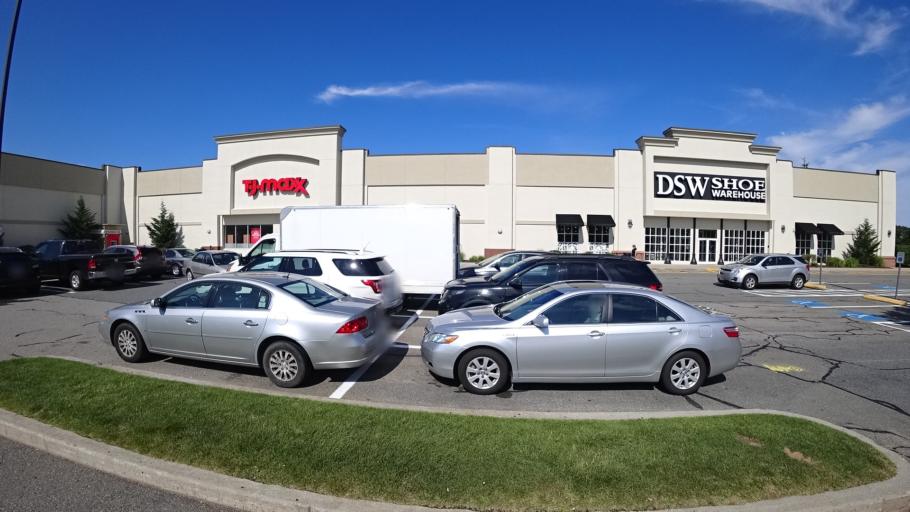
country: US
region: Massachusetts
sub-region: Norfolk County
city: Dedham
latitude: 42.2547
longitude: -71.1685
